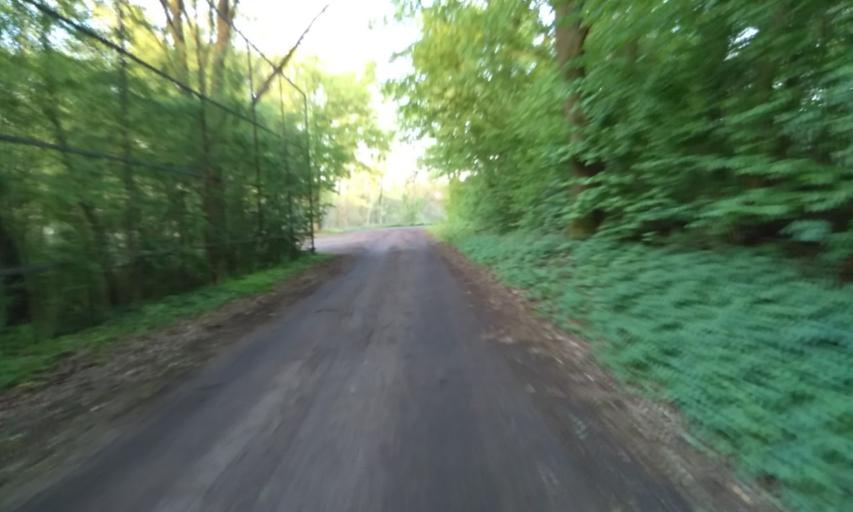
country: DE
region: Lower Saxony
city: Bargstedt
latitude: 53.4527
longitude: 9.4546
